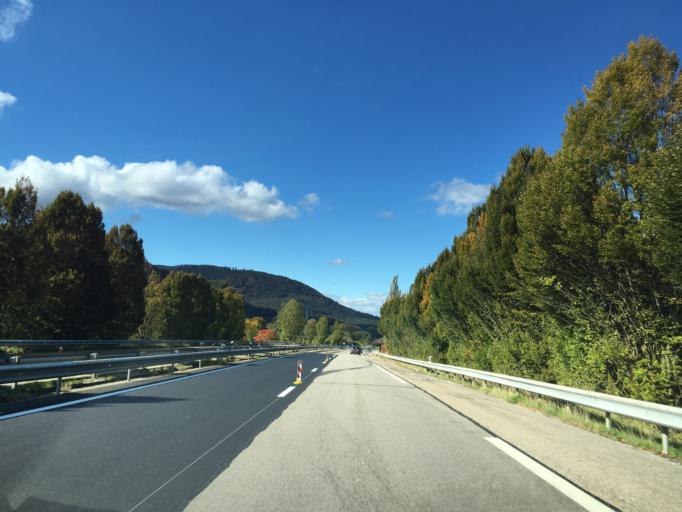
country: FR
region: Lorraine
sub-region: Departement des Vosges
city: Etival-Clairefontaine
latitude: 48.3732
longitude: 6.8791
